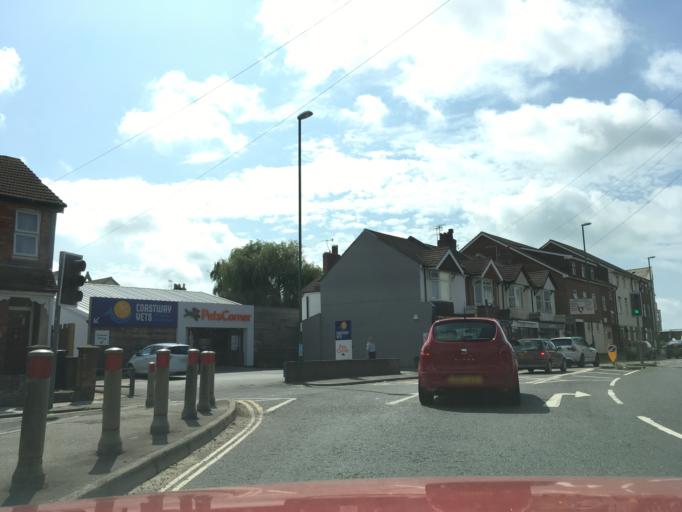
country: GB
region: England
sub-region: West Sussex
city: Shoreham-by-Sea
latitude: 50.8336
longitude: -0.2787
